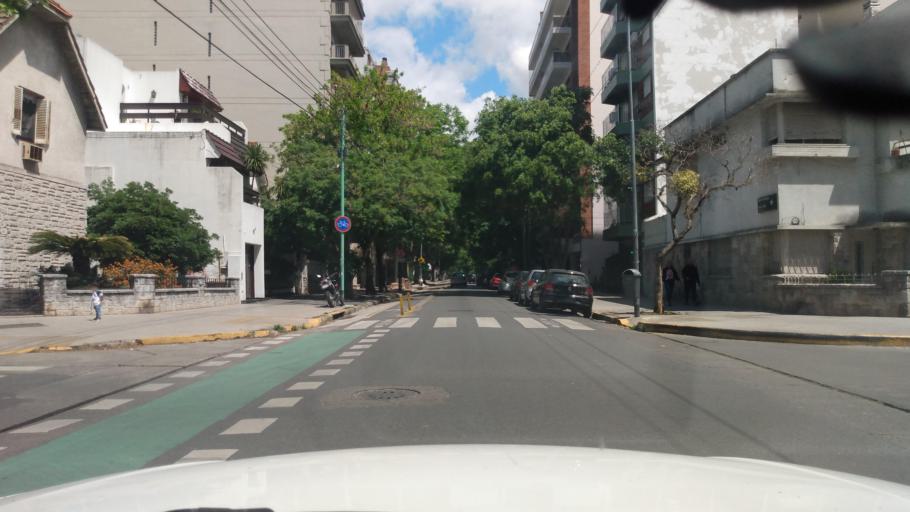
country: AR
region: Buenos Aires F.D.
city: Villa Santa Rita
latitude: -34.5777
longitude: -58.4902
